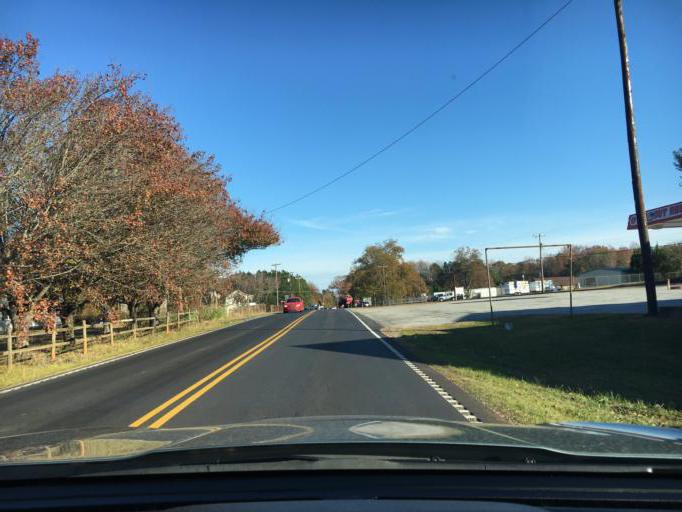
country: US
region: South Carolina
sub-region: Spartanburg County
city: Inman
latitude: 34.9976
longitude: -82.0571
